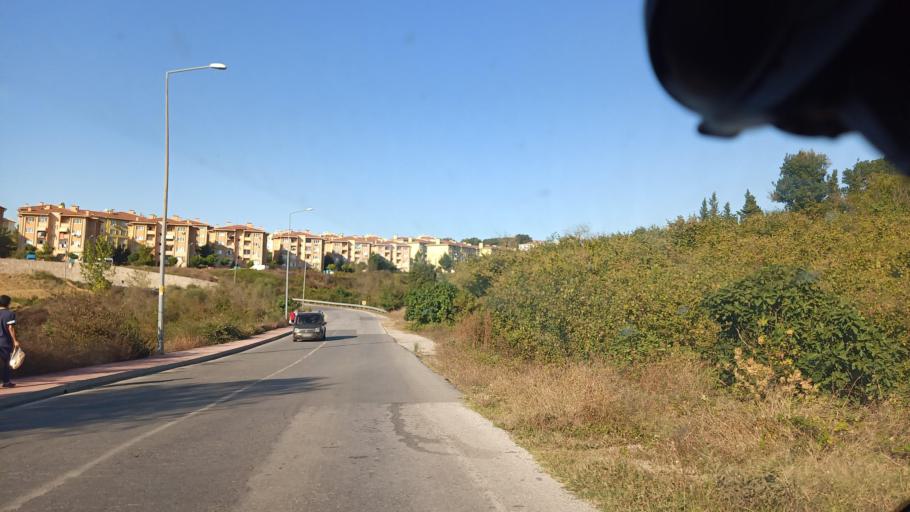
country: TR
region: Kocaeli
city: Kaymaz
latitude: 40.8590
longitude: 30.2779
